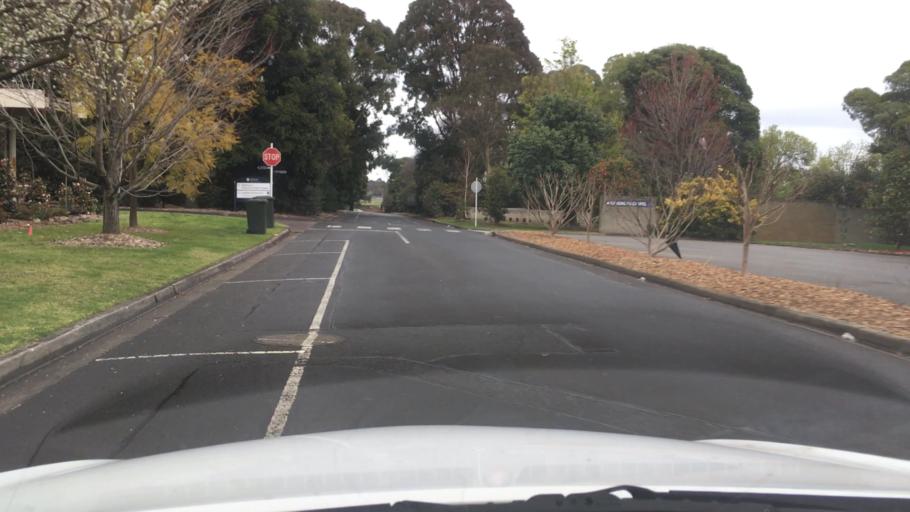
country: AU
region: Victoria
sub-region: Greater Dandenong
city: Noble Park North
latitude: -37.9441
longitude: 145.1732
